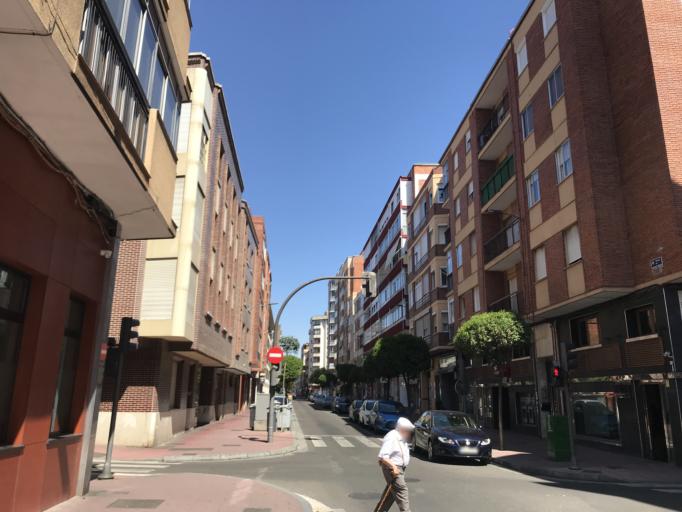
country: ES
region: Castille and Leon
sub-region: Provincia de Valladolid
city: Valladolid
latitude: 41.6505
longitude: -4.7161
